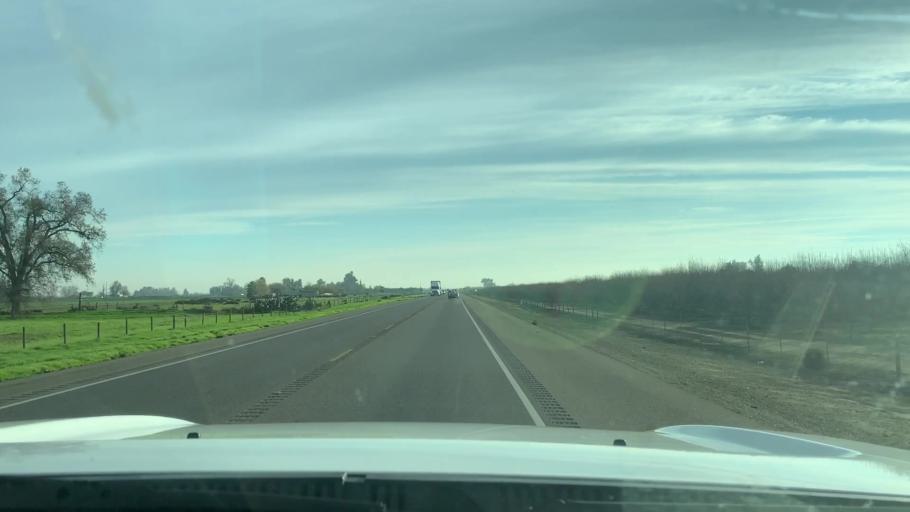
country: US
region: California
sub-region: Fresno County
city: Riverdale
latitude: 36.4211
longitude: -119.8033
